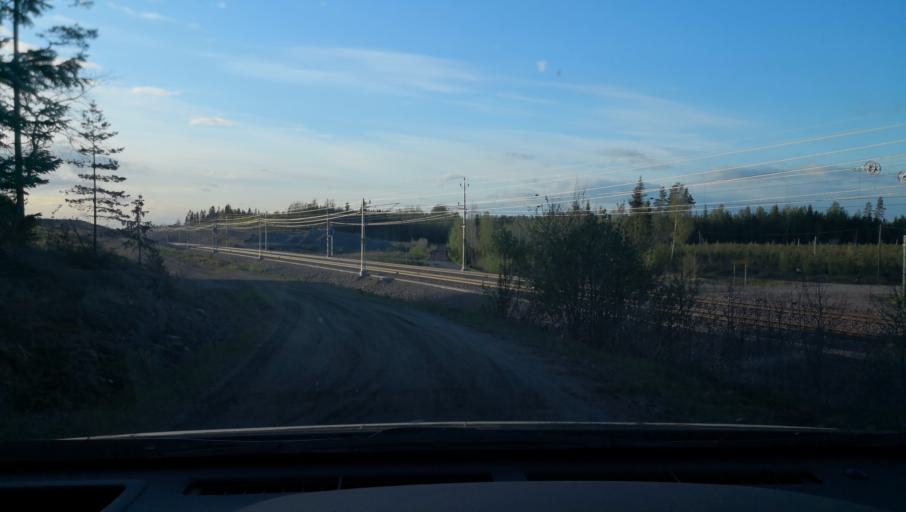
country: SE
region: OErebro
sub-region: Askersunds Kommun
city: Asbro
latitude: 58.8781
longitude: 15.1434
